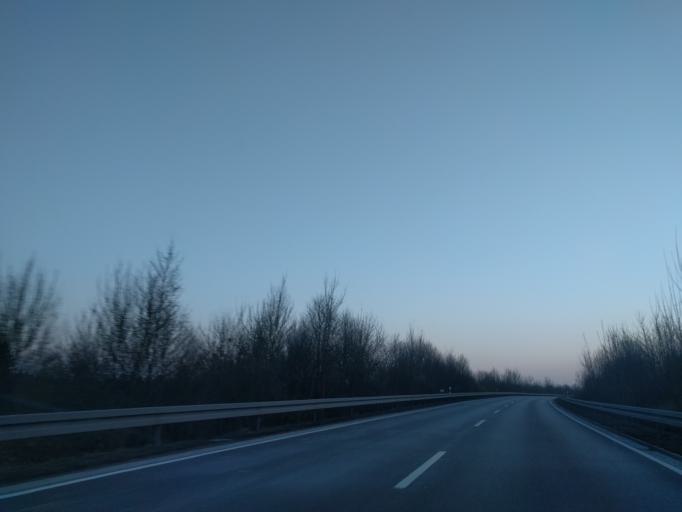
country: DE
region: Bavaria
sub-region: Swabia
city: Genderkingen
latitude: 48.6990
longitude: 10.8886
